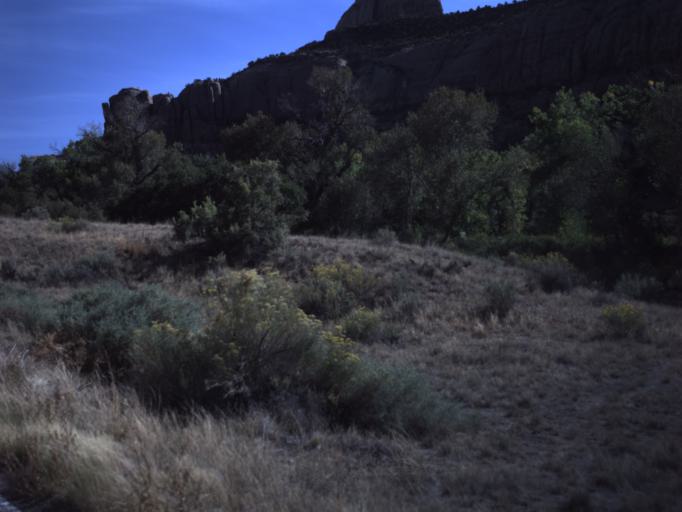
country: US
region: Utah
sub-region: San Juan County
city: Monticello
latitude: 38.0369
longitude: -109.5483
